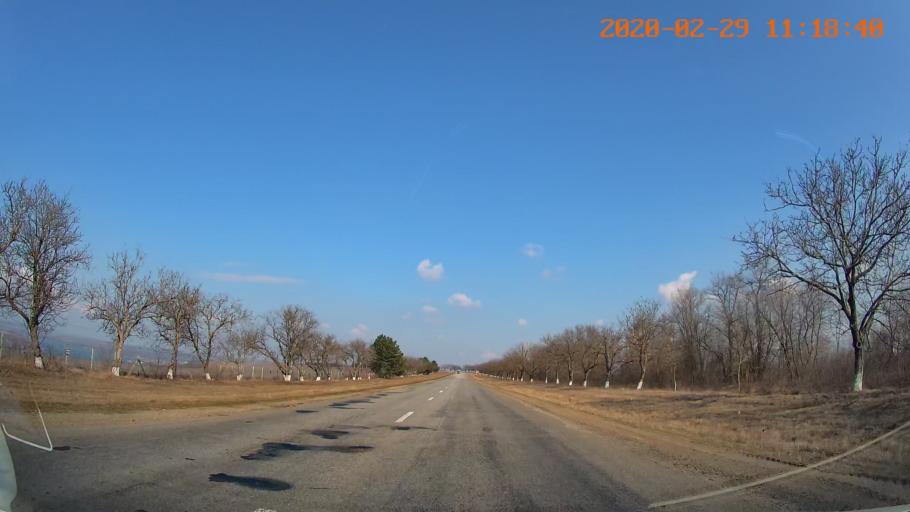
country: MD
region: Telenesti
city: Cocieri
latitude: 47.3383
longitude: 29.1746
